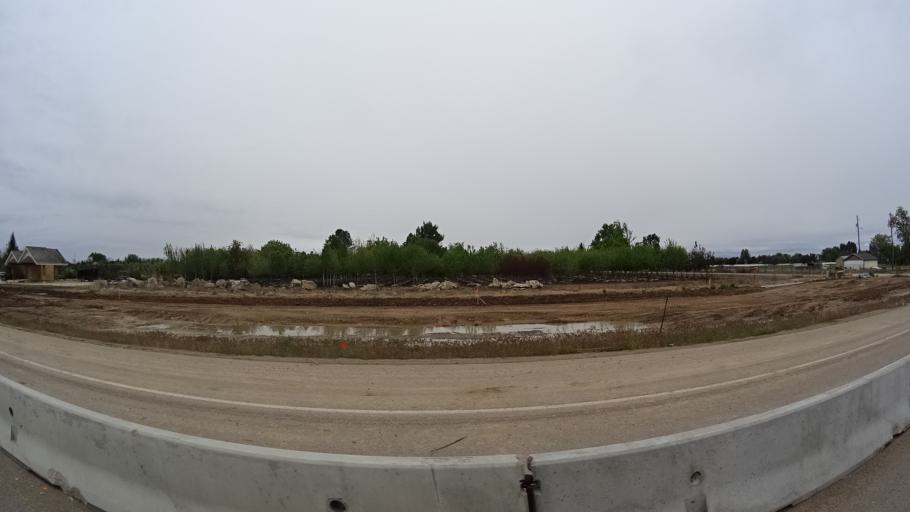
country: US
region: Idaho
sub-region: Ada County
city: Star
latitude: 43.6630
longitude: -116.4630
